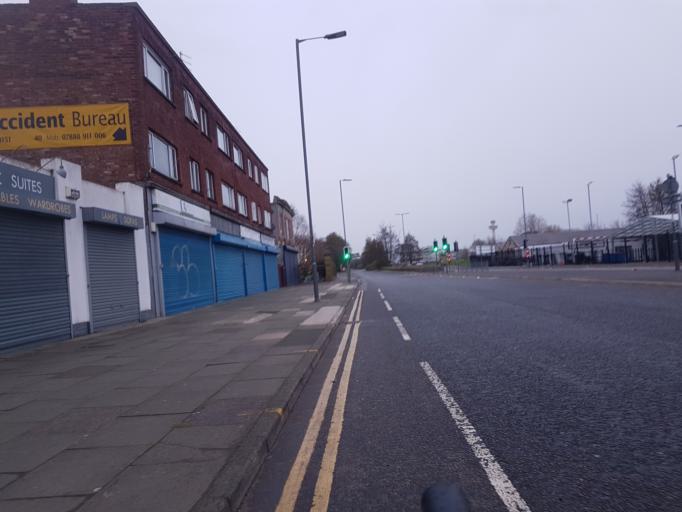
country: GB
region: England
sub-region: Liverpool
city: Liverpool
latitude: 53.4205
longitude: -2.9781
